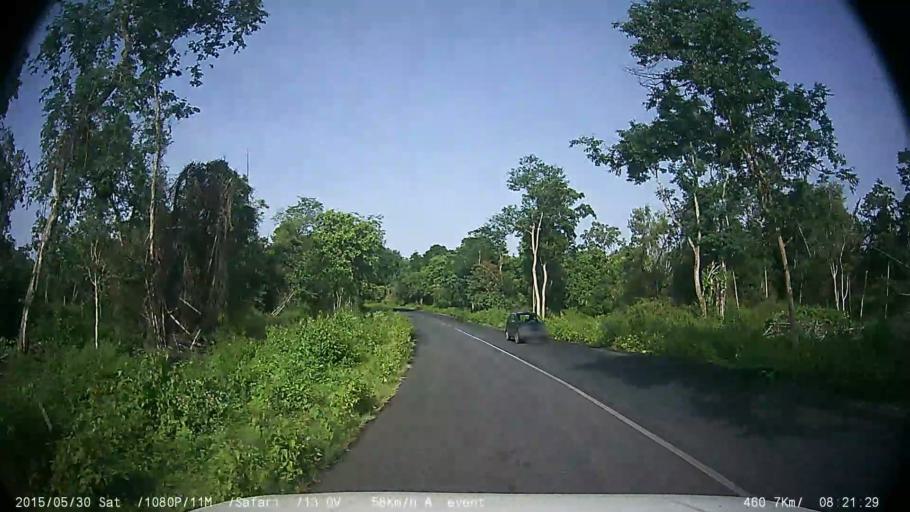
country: IN
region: Karnataka
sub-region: Chamrajnagar
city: Gundlupet
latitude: 11.7651
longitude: 76.5231
